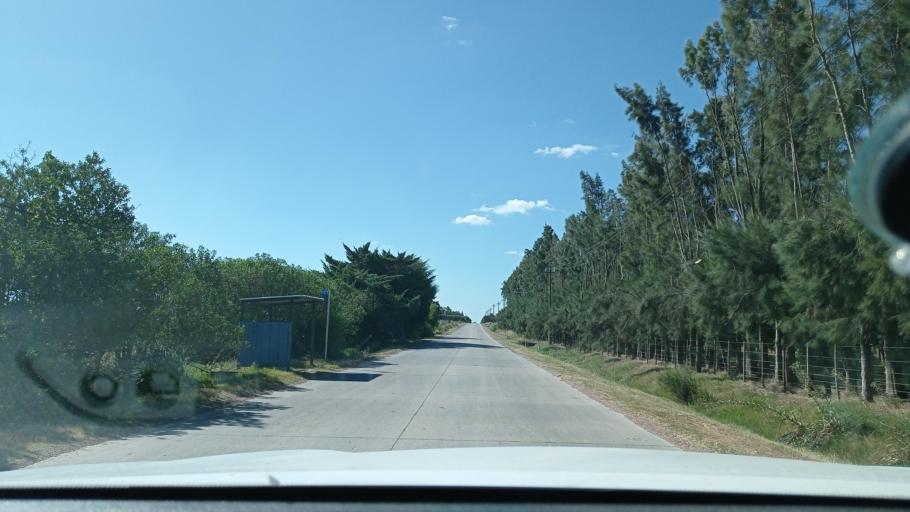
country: UY
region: Canelones
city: La Paz
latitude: -34.7785
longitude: -56.2564
